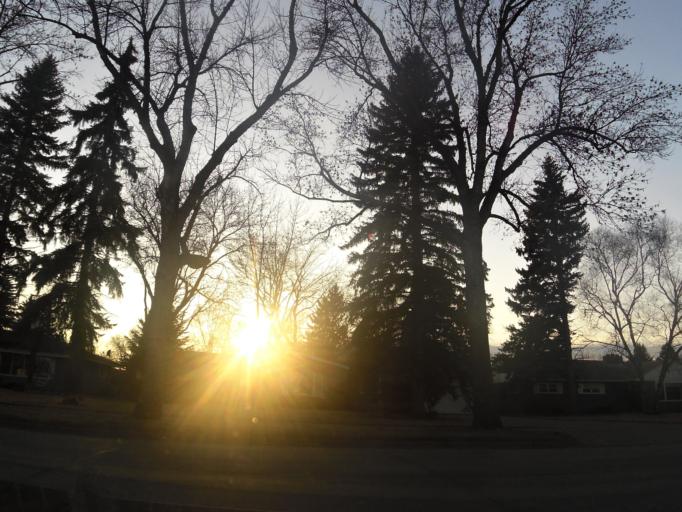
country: US
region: North Dakota
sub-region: Grand Forks County
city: Grand Forks
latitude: 47.8980
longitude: -97.0289
